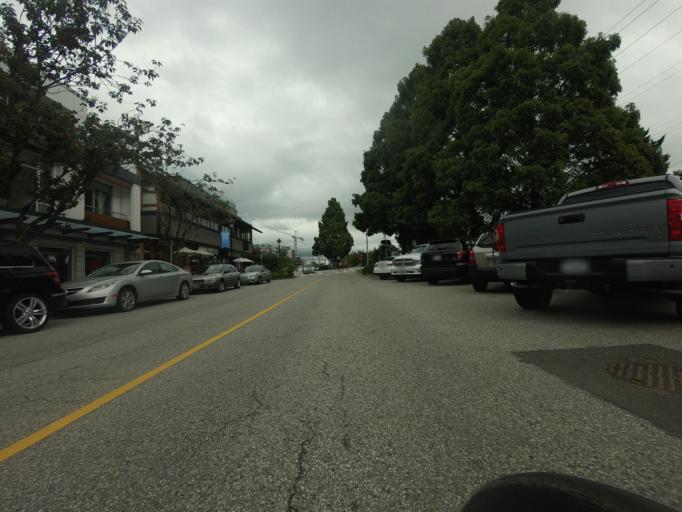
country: CA
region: British Columbia
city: West Vancouver
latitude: 49.3275
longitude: -123.1575
